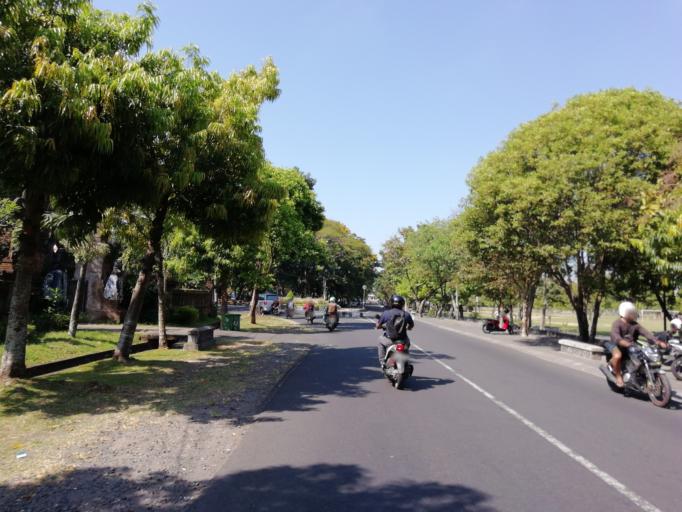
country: ID
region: Bali
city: Banjar Batanpoh
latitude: -8.6698
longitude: 115.2357
